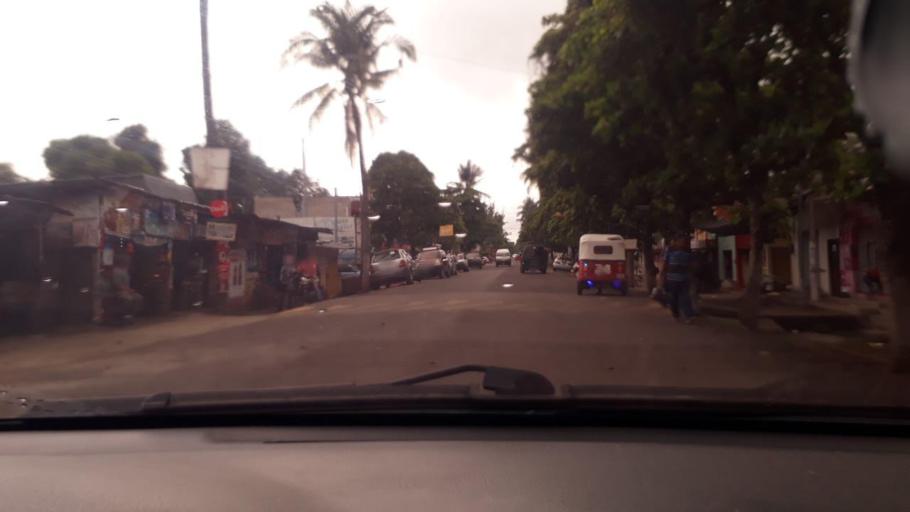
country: GT
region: Jutiapa
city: Jalpatagua
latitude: 14.1352
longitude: -90.0097
